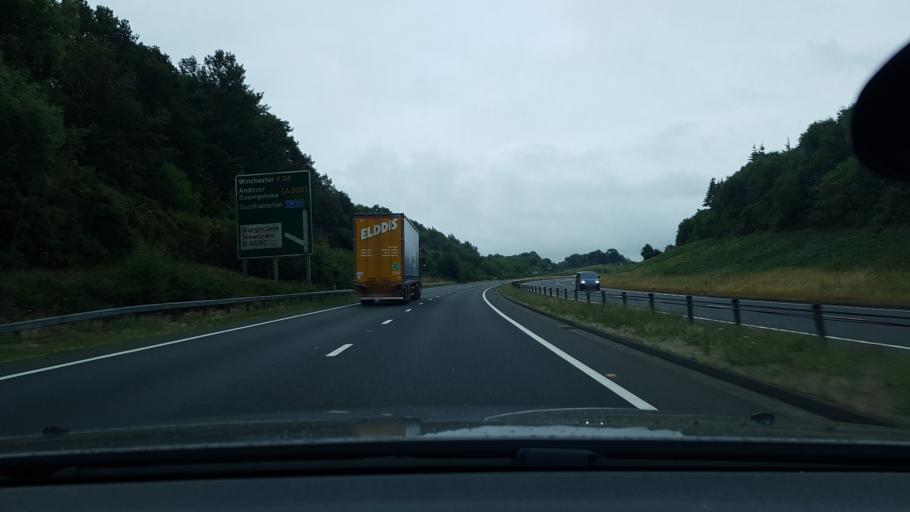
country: GB
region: England
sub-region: Hampshire
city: Highclere
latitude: 51.3540
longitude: -1.3407
